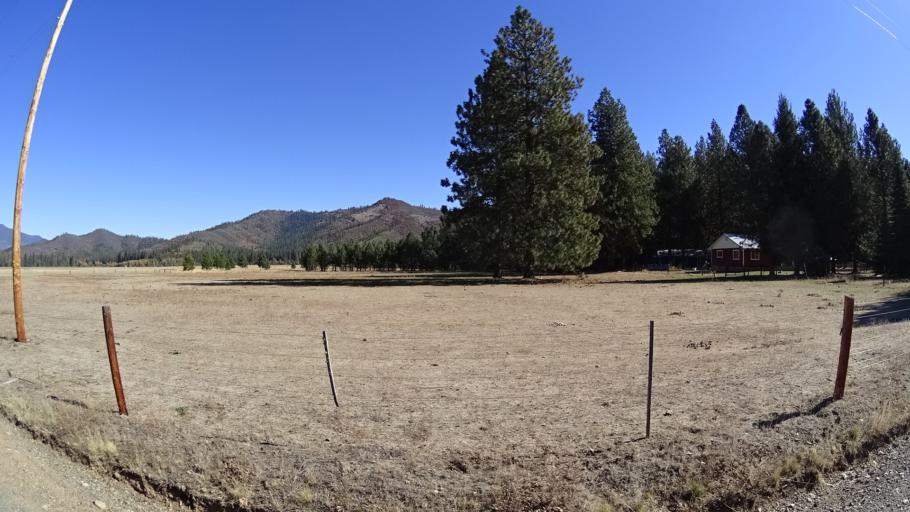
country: US
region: California
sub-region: Siskiyou County
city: Yreka
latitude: 41.5845
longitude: -122.9747
